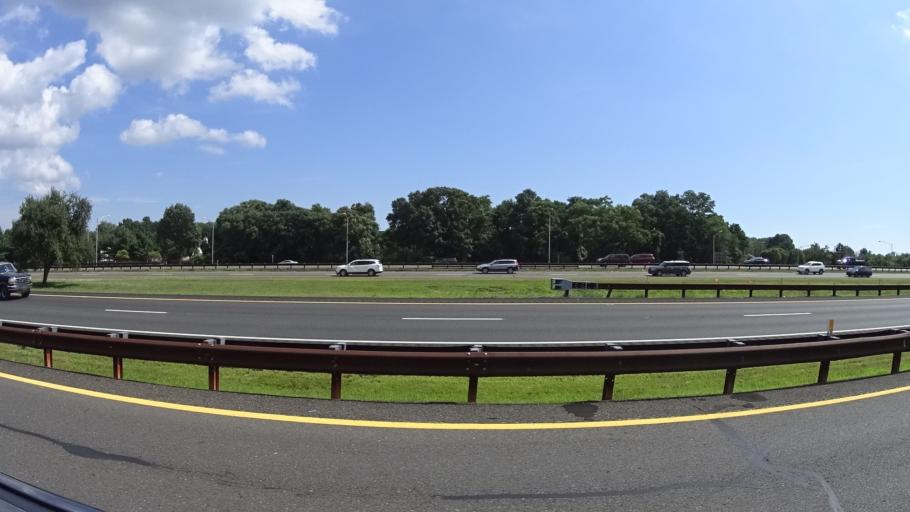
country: US
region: New Jersey
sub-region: Monmouth County
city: Lincroft
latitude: 40.3385
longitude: -74.1018
